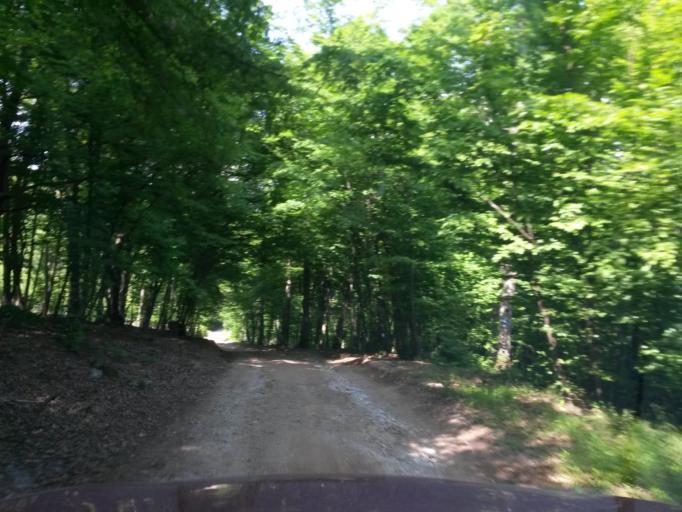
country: SK
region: Kosicky
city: Moldava nad Bodvou
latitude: 48.6446
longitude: 20.9579
